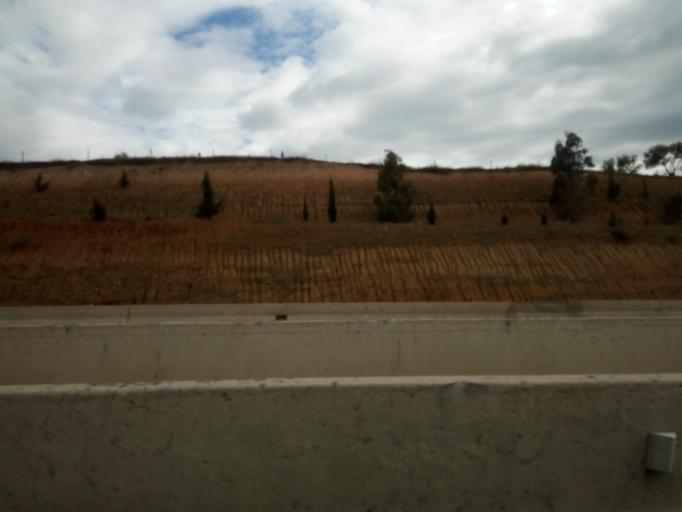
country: DZ
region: Bouira
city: Chorfa
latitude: 36.3157
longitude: 4.1583
